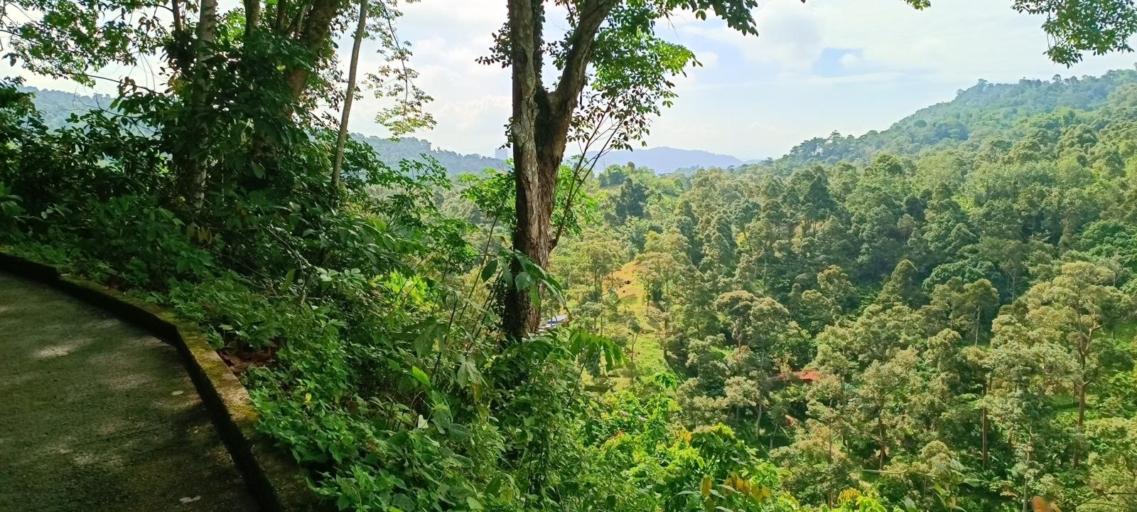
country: MY
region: Penang
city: Kampung Sungai Ara
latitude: 5.3226
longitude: 100.2437
